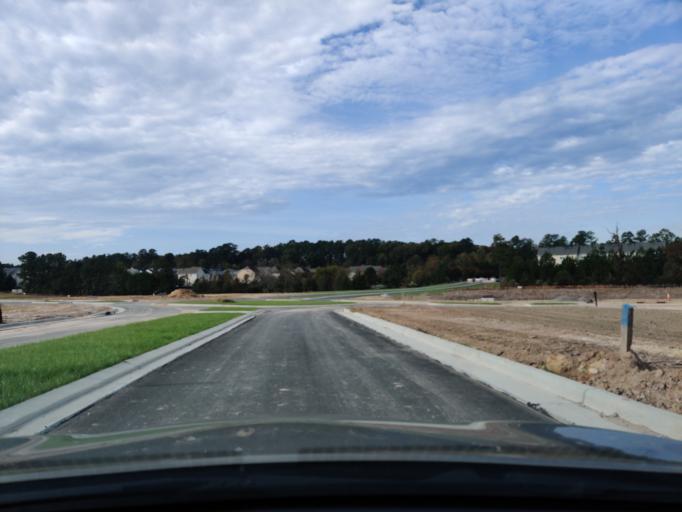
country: US
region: North Carolina
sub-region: Wake County
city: Morrisville
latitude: 35.8282
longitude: -78.8572
